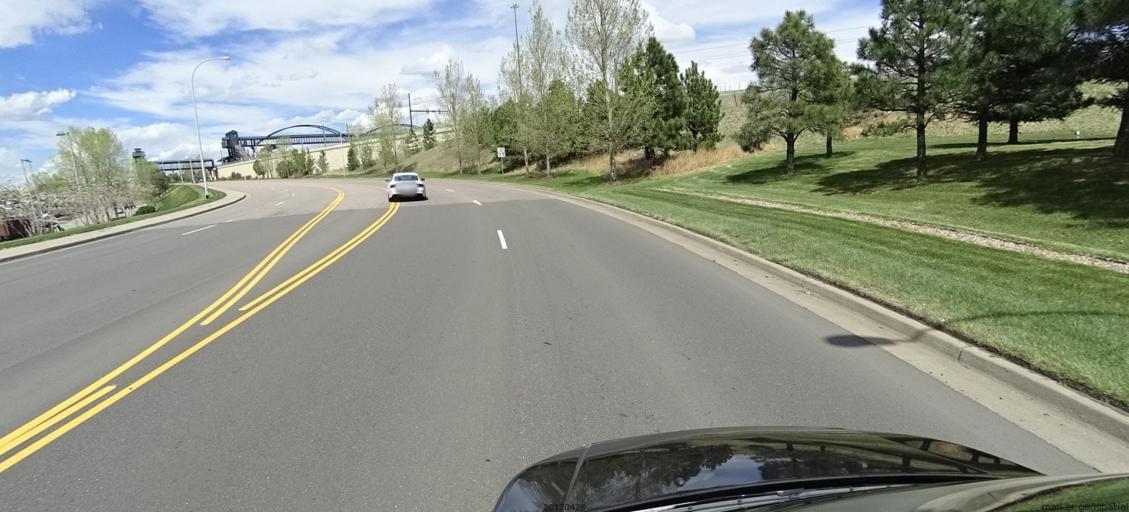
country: US
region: Colorado
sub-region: Adams County
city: Lone Tree
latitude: 39.5592
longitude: -104.8730
